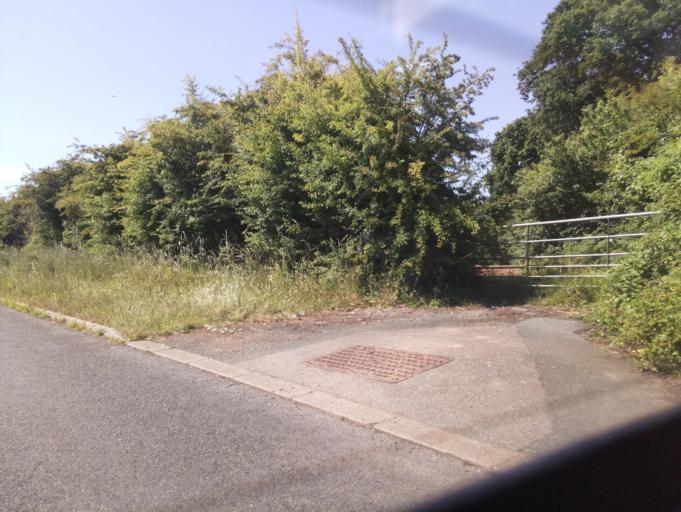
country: GB
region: England
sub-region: Devon
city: Marldon
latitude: 50.4558
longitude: -3.5776
